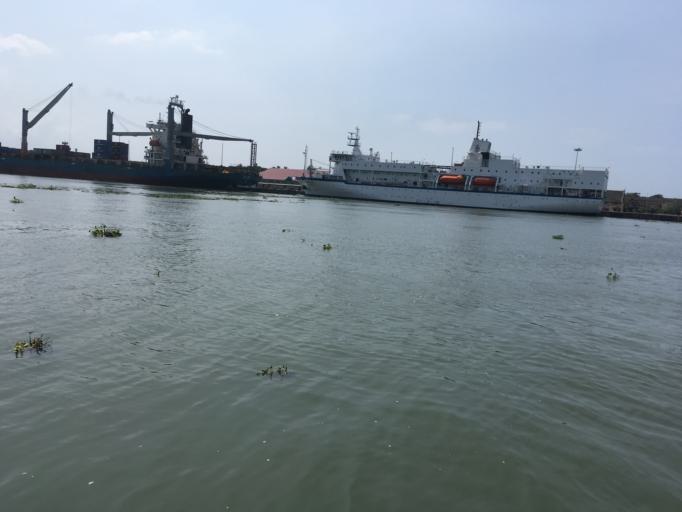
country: IN
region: Kerala
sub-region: Ernakulam
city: Cochin
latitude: 9.9698
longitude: 76.2680
